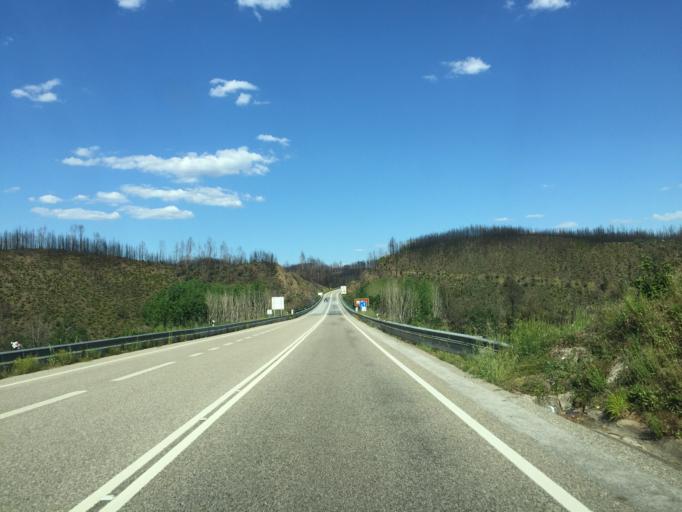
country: PT
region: Leiria
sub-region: Pedrogao Grande
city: Pedrogao Grande
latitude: 39.9268
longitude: -8.1933
